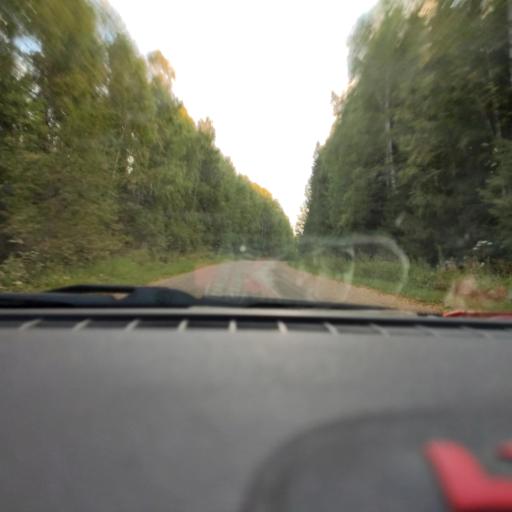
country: RU
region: Perm
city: Pavlovskiy
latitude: 57.9887
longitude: 54.8740
